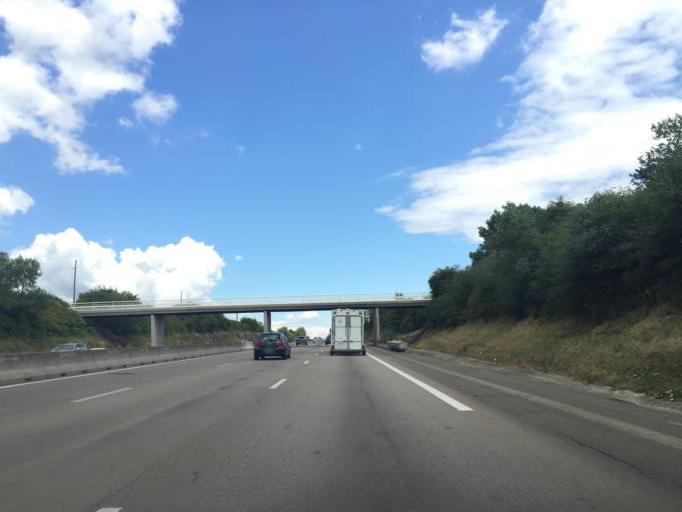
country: FR
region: Rhone-Alpes
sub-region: Departement de l'Isere
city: Auberives-sur-Vareze
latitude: 45.4374
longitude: 4.8252
